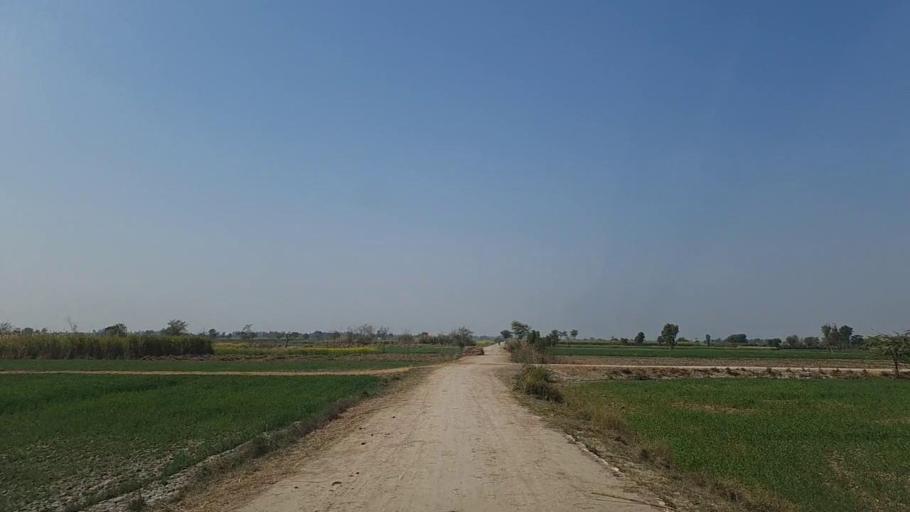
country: PK
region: Sindh
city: Daur
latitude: 26.4413
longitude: 68.2985
